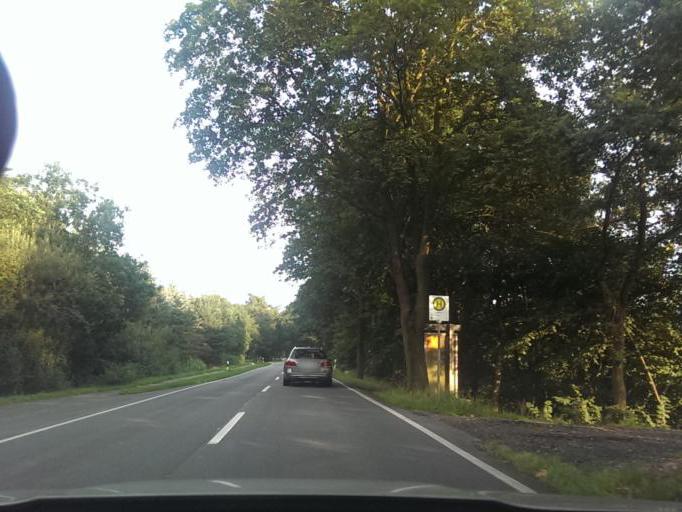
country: DE
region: Lower Saxony
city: Lilienthal
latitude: 53.1820
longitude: 8.8745
